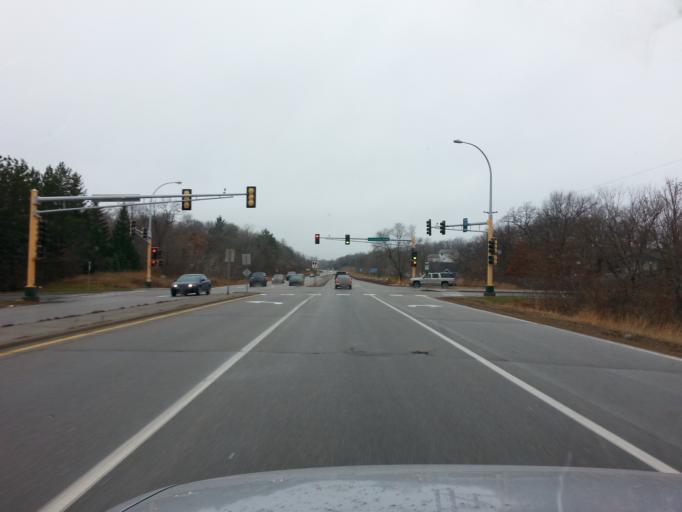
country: US
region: Minnesota
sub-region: Scott County
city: Prior Lake
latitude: 44.7260
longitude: -93.4032
